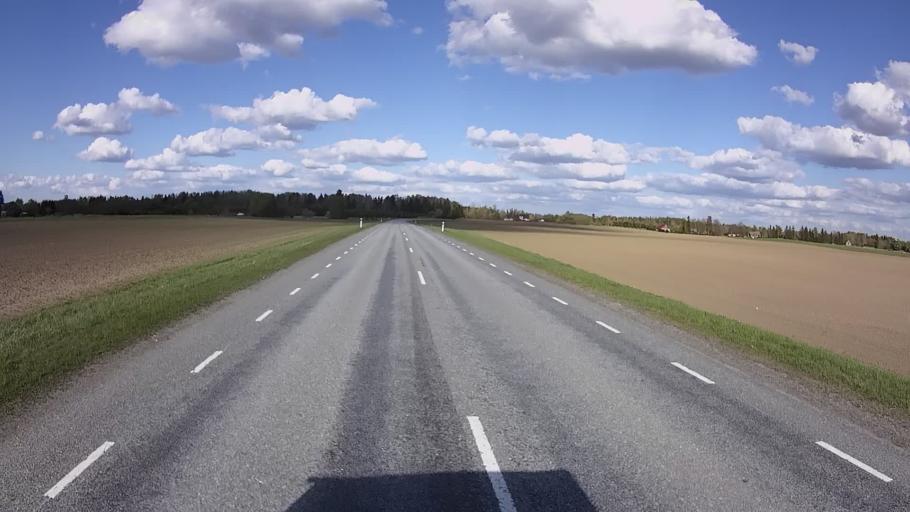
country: EE
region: Jogevamaa
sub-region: Poltsamaa linn
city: Poltsamaa
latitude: 58.6763
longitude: 26.0184
